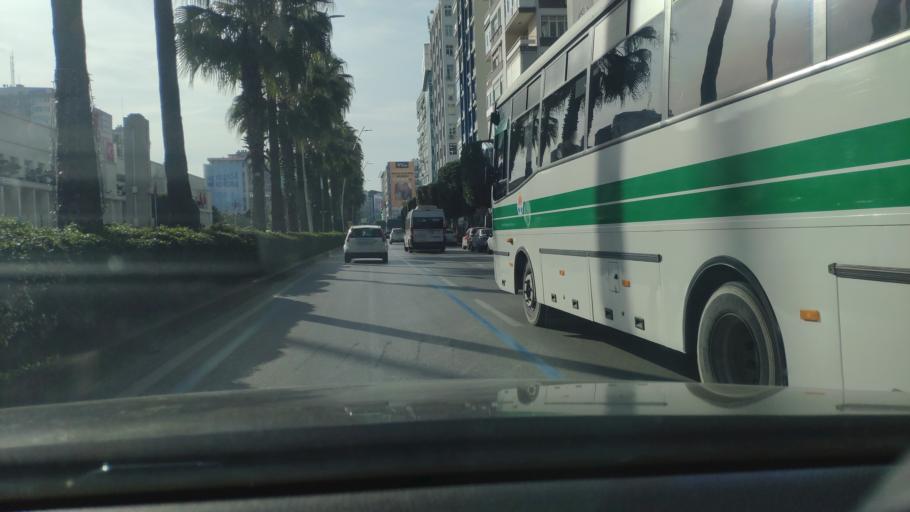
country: TR
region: Adana
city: Adana
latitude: 36.9939
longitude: 35.3252
